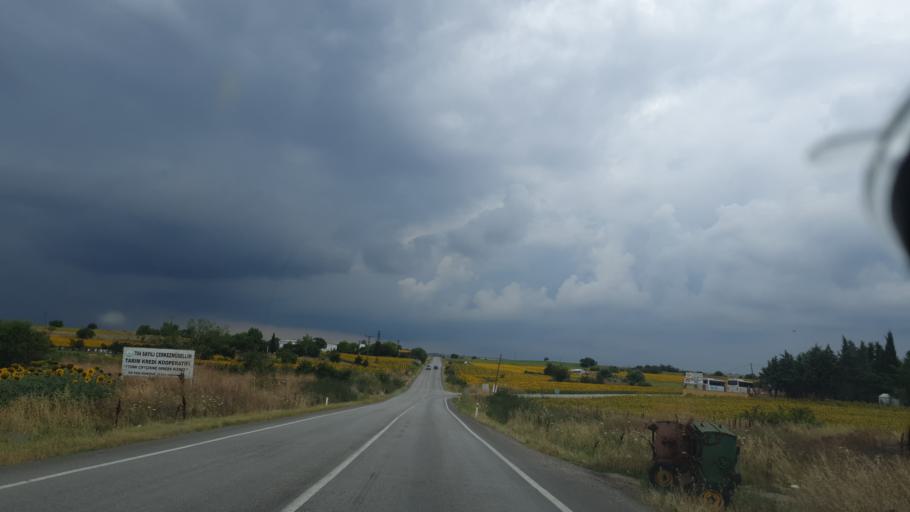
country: TR
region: Tekirdag
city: Hayrabolu
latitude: 41.2193
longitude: 27.0765
